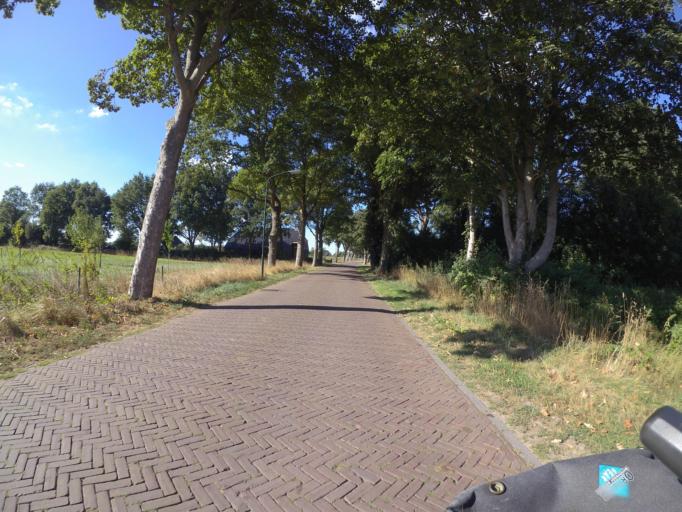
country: NL
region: Drenthe
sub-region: Gemeente Aa en Hunze
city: Anloo
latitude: 53.0039
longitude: 6.6808
